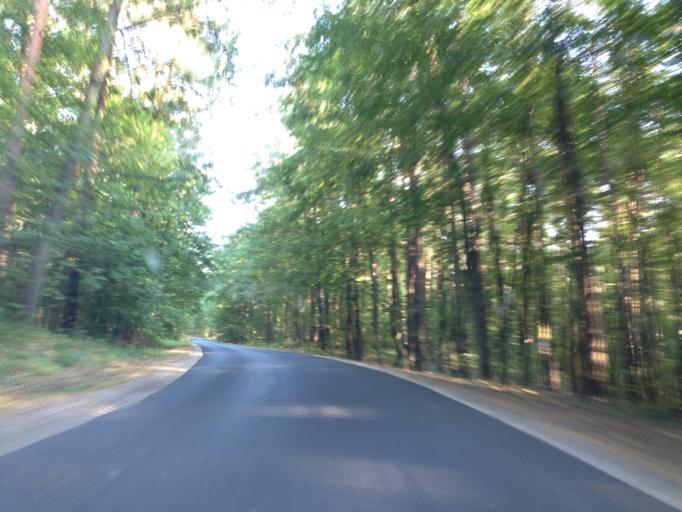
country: PL
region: Kujawsko-Pomorskie
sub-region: Powiat brodnicki
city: Brodnica
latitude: 53.3608
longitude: 19.3815
